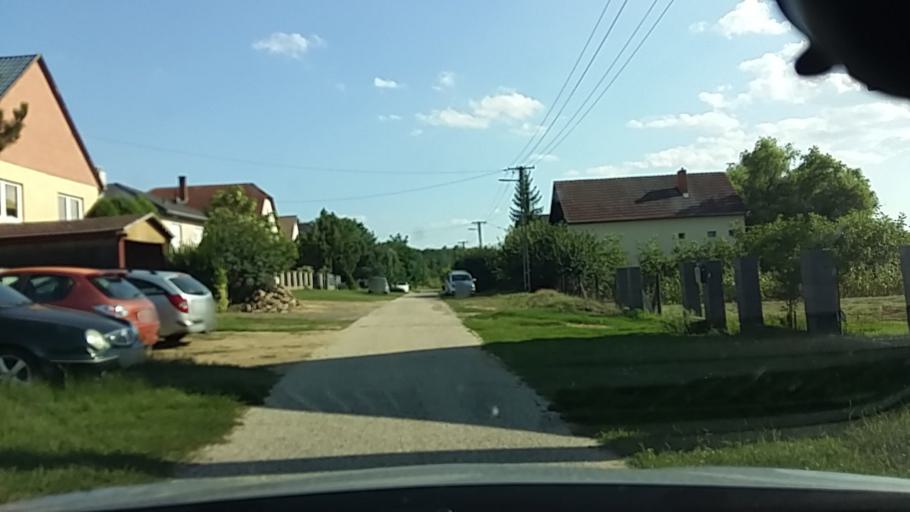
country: HU
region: Szabolcs-Szatmar-Bereg
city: Nyirbogdany
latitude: 48.0815
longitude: 21.8607
